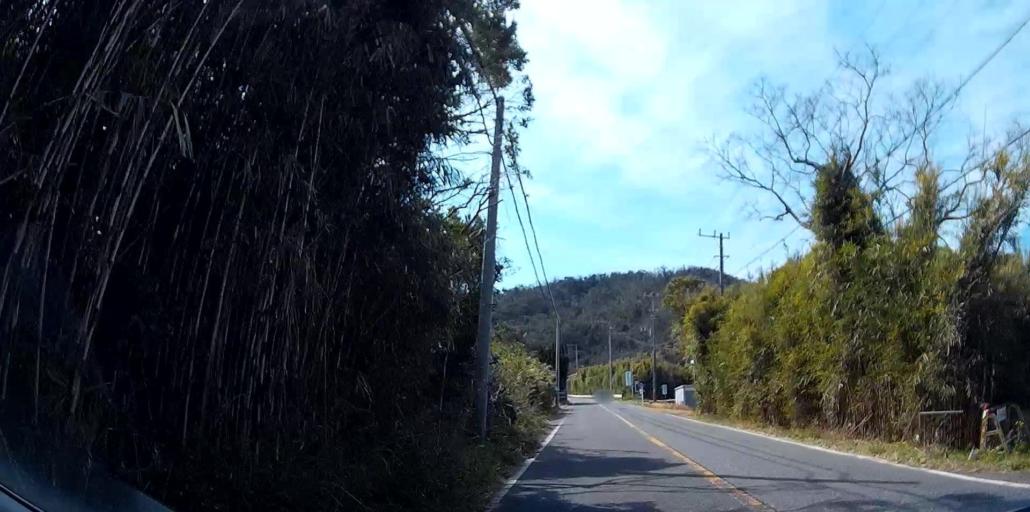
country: JP
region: Chiba
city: Tateyama
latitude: 34.9751
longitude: 139.7712
